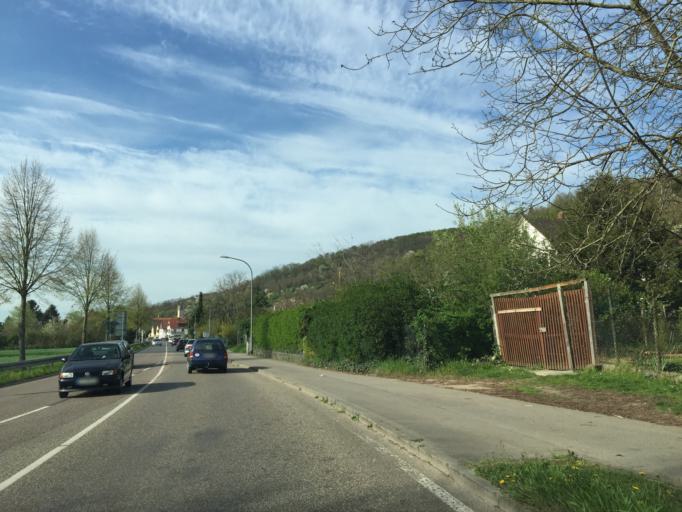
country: DE
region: Baden-Wuerttemberg
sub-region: Karlsruhe Region
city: Hemsbach
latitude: 49.5725
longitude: 8.6631
